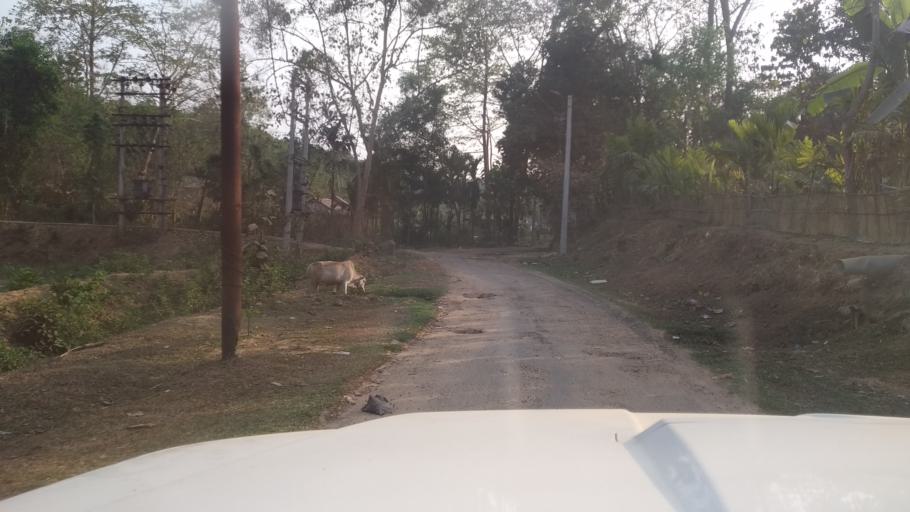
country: IN
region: Tripura
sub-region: West Tripura
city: Sonamura
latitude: 23.3479
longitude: 91.3214
